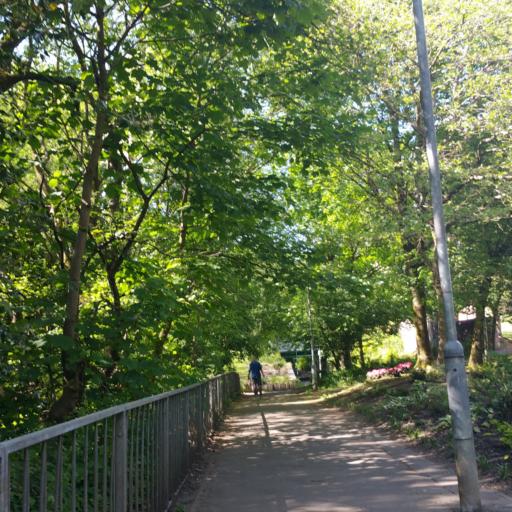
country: GB
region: Scotland
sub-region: East Dunbartonshire
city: Milngavie
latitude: 55.9424
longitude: -4.3185
